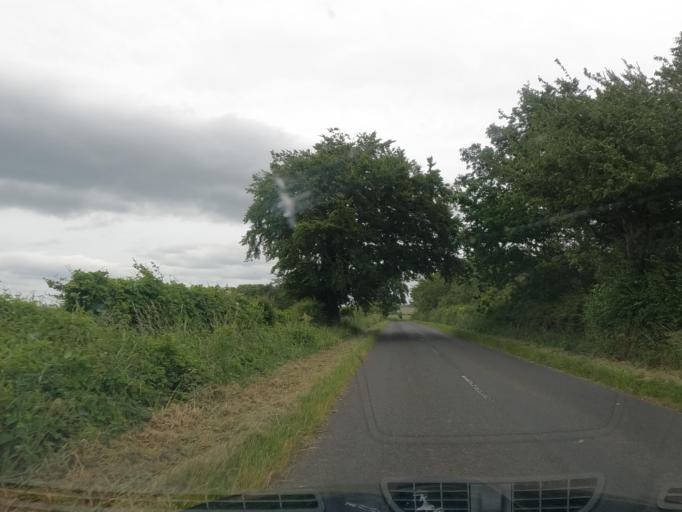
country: GB
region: England
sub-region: Northumberland
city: Doddington
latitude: 55.5633
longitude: -1.9270
